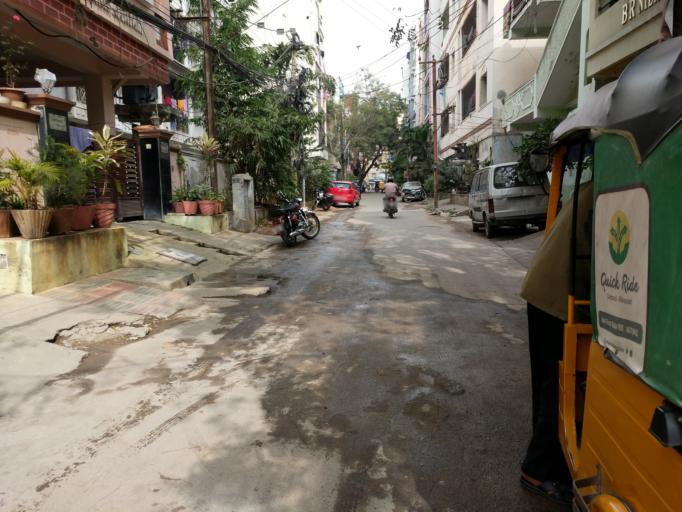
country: IN
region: Telangana
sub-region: Rangareddi
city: Kukatpalli
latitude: 17.4626
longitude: 78.3663
